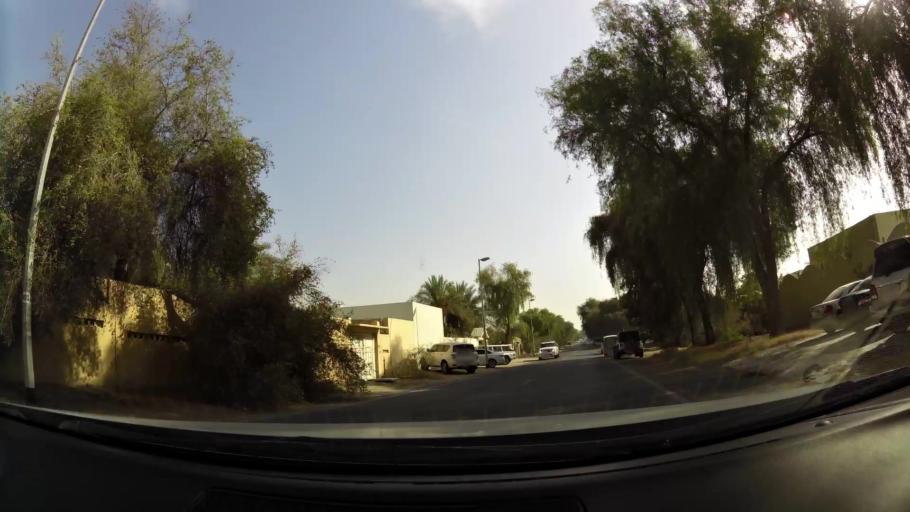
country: AE
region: Ash Shariqah
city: Sharjah
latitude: 25.2201
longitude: 55.3965
